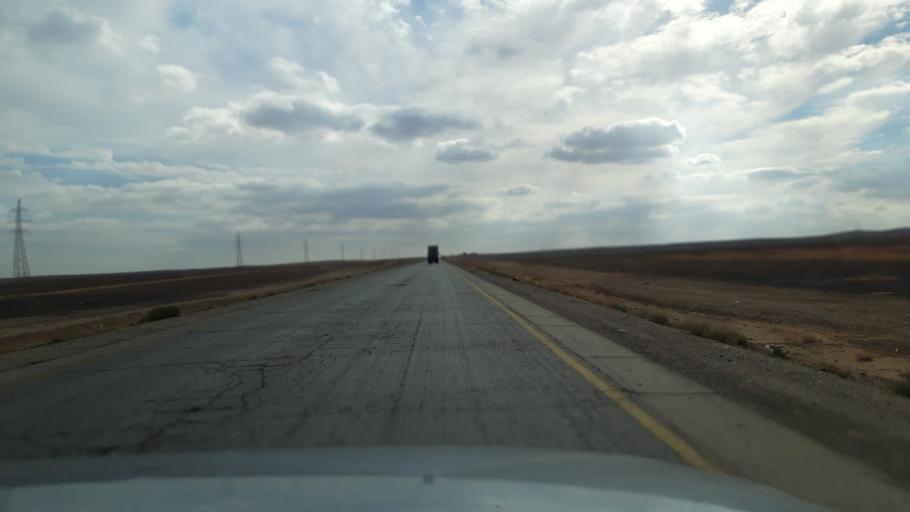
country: JO
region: Amman
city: Al Azraq ash Shamali
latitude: 31.7619
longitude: 36.5539
